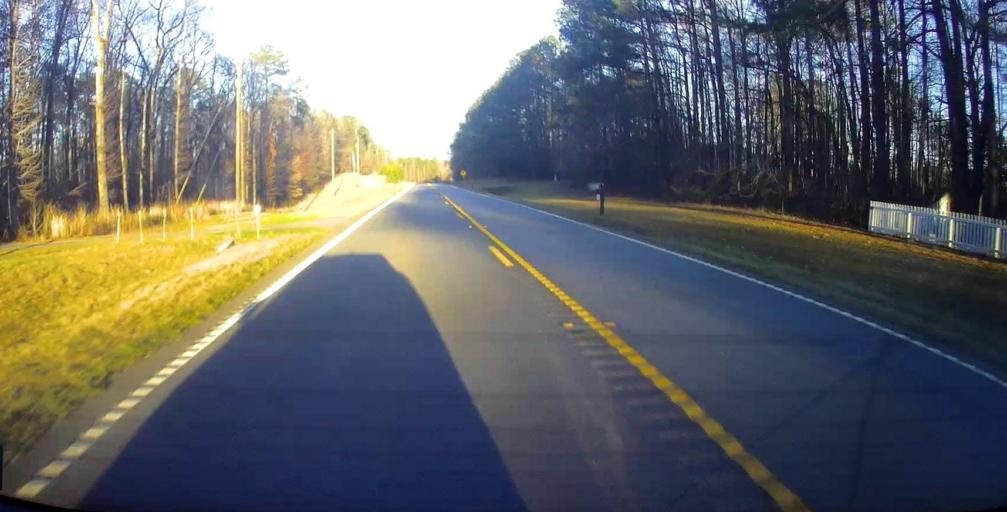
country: US
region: Georgia
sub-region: Harris County
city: Hamilton
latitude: 32.6727
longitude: -84.9304
